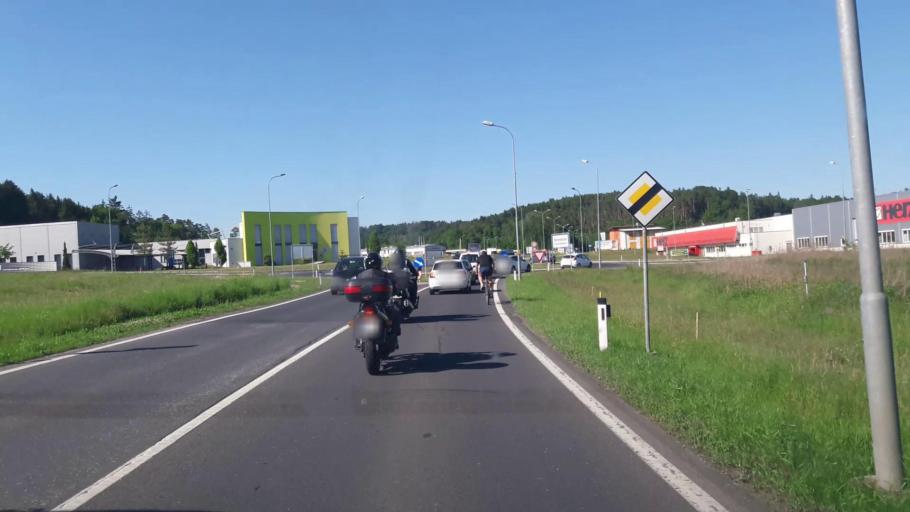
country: AT
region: Burgenland
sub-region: Politischer Bezirk Oberwart
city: Kemeten
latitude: 47.2720
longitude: 16.1532
